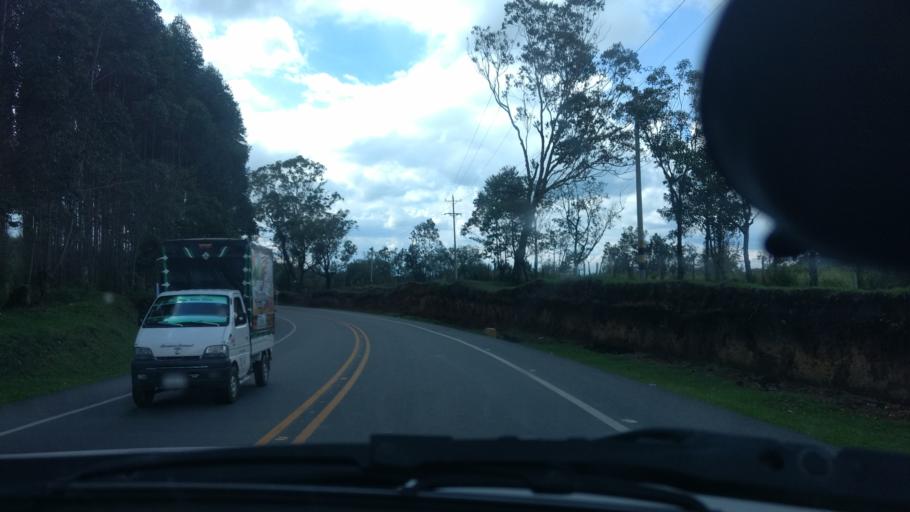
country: CO
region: Cauca
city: Popayan
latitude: 2.5175
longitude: -76.5443
